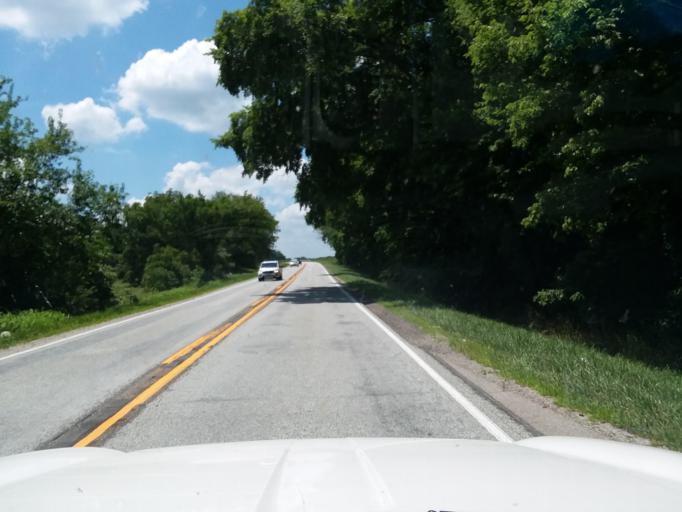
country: US
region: Indiana
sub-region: Johnson County
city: Trafalgar
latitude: 39.3842
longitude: -86.2354
